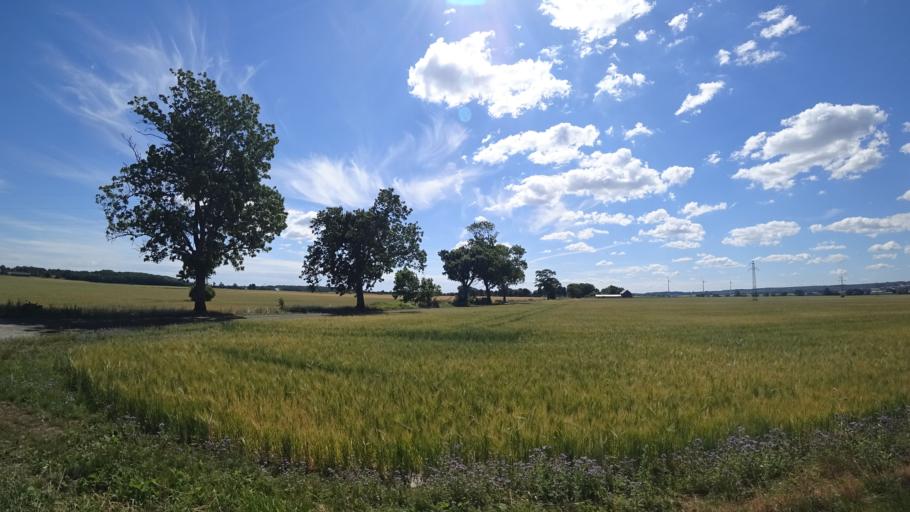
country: SE
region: Skane
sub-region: Kristianstads Kommun
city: Onnestad
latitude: 56.0690
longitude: 14.0644
